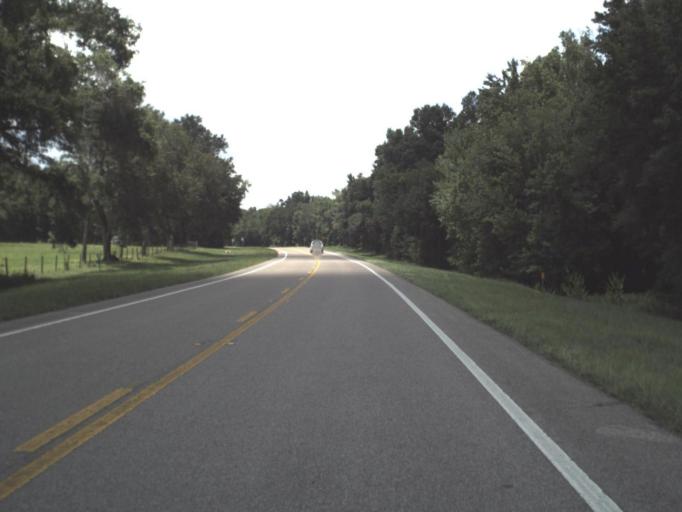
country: US
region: Florida
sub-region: Hernando County
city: North Brooksville
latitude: 28.6093
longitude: -82.4023
